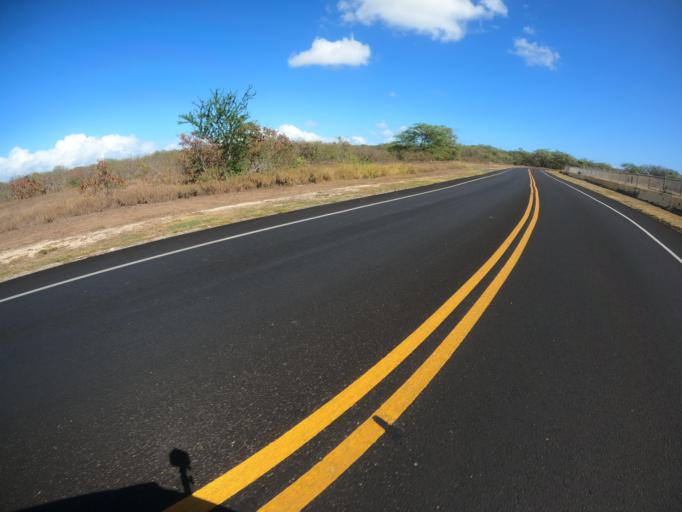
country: US
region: Hawaii
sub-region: Honolulu County
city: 'Ewa Villages
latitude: 21.3155
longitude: -158.0564
